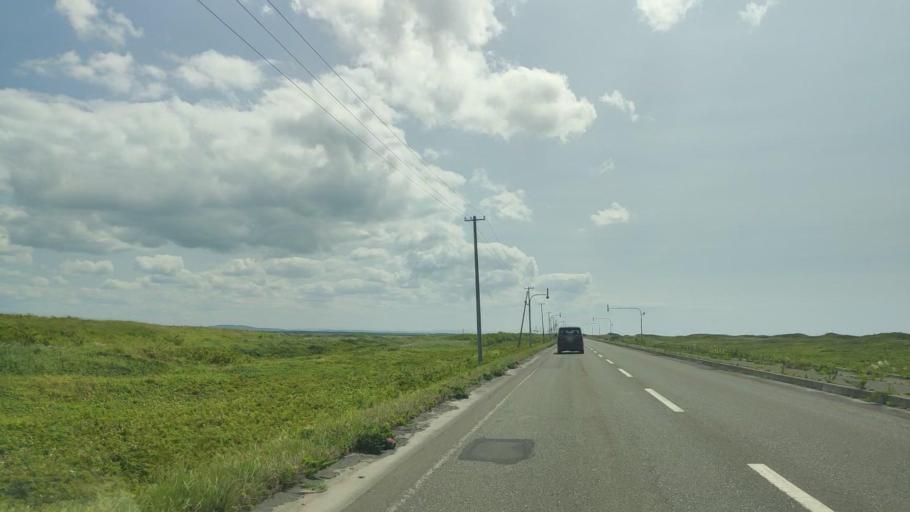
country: JP
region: Hokkaido
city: Makubetsu
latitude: 44.9324
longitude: 141.7192
